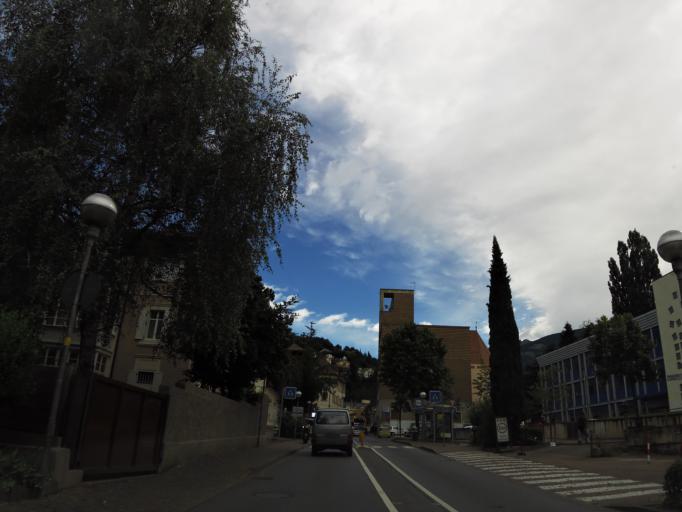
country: IT
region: Trentino-Alto Adige
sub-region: Bolzano
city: Merano
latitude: 46.6678
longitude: 11.1628
